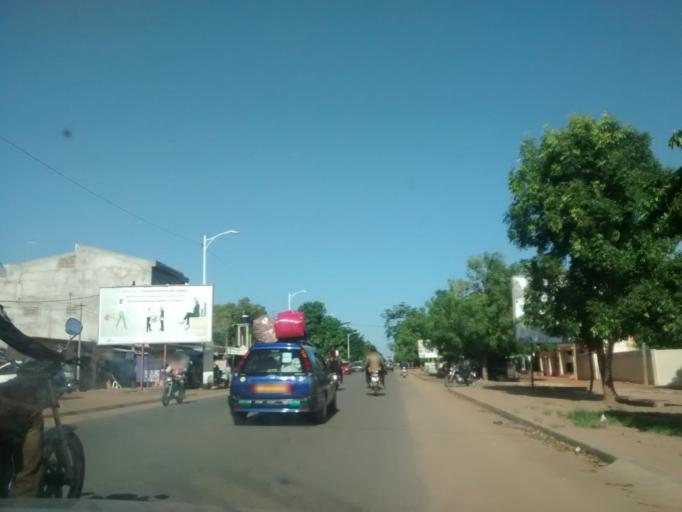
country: TG
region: Maritime
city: Lome
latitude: 6.1727
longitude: 1.1875
